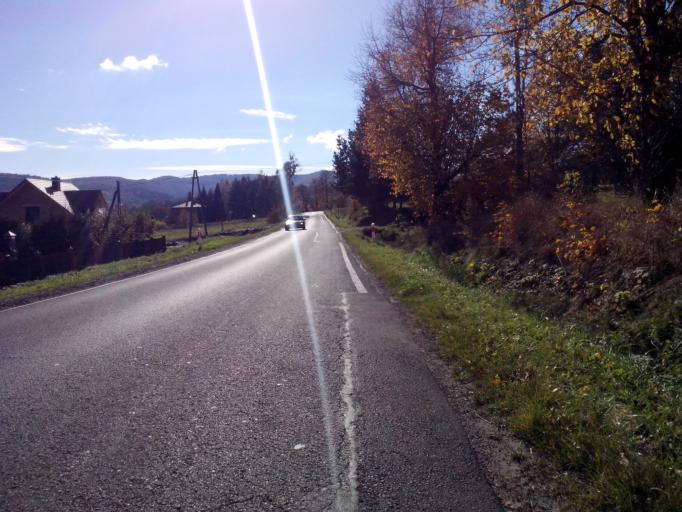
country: PL
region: Subcarpathian Voivodeship
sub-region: Powiat strzyzowski
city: Jawornik
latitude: 49.7880
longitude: 21.8567
